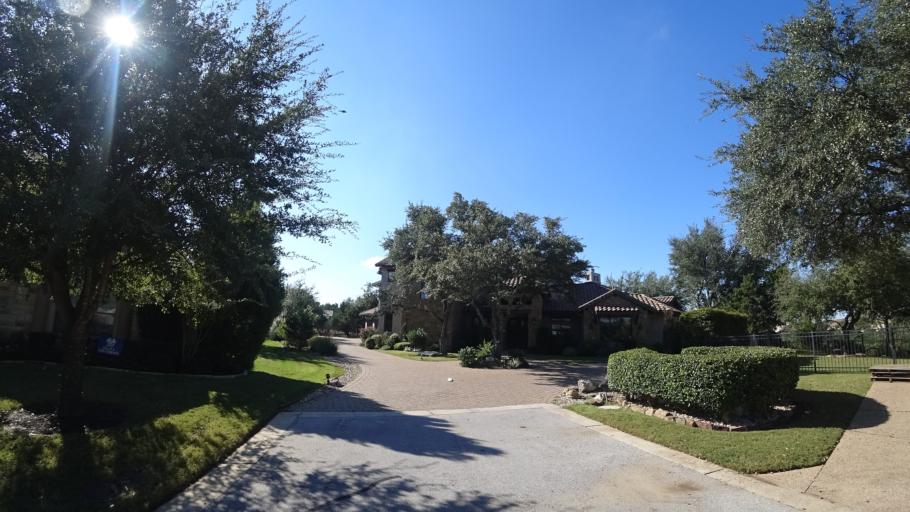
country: US
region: Texas
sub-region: Travis County
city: Barton Creek
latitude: 30.3487
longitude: -97.8885
